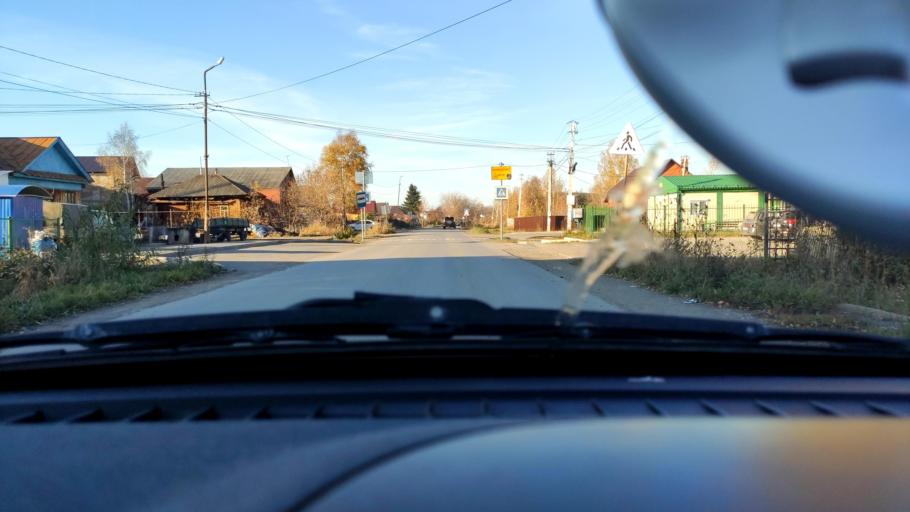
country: RU
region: Perm
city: Froly
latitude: 57.8859
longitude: 56.2576
